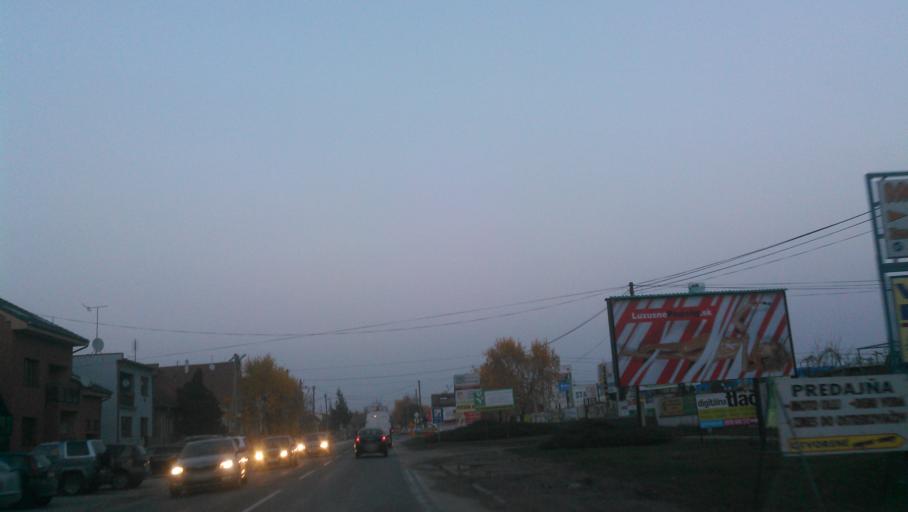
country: SK
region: Bratislavsky
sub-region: Okres Pezinok
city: Pezinok
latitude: 48.2797
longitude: 17.2594
